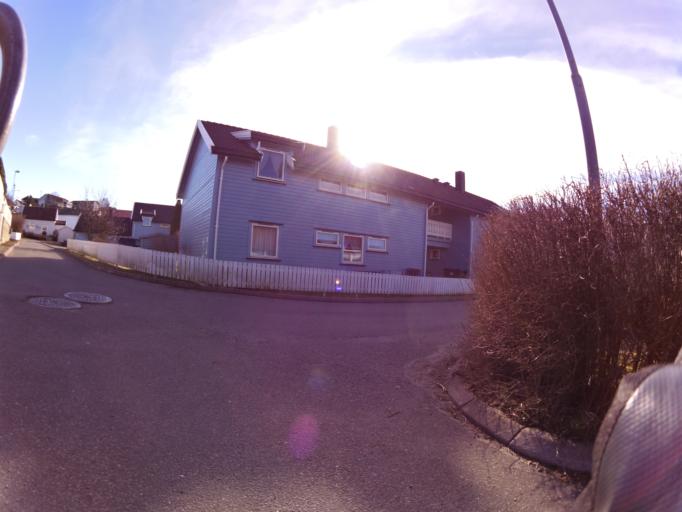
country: NO
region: Ostfold
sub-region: Fredrikstad
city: Fredrikstad
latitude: 59.2154
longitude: 10.9051
